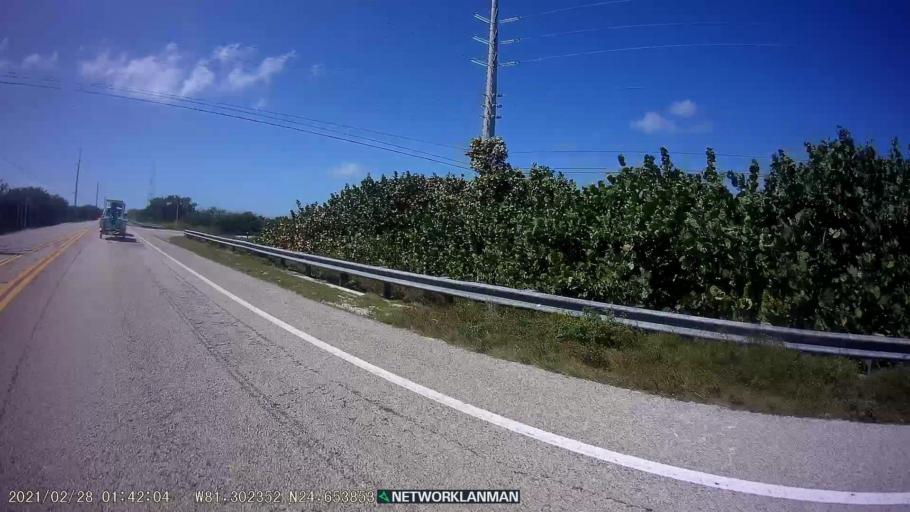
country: US
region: Florida
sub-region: Monroe County
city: Big Pine Key
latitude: 24.6547
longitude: -81.3018
